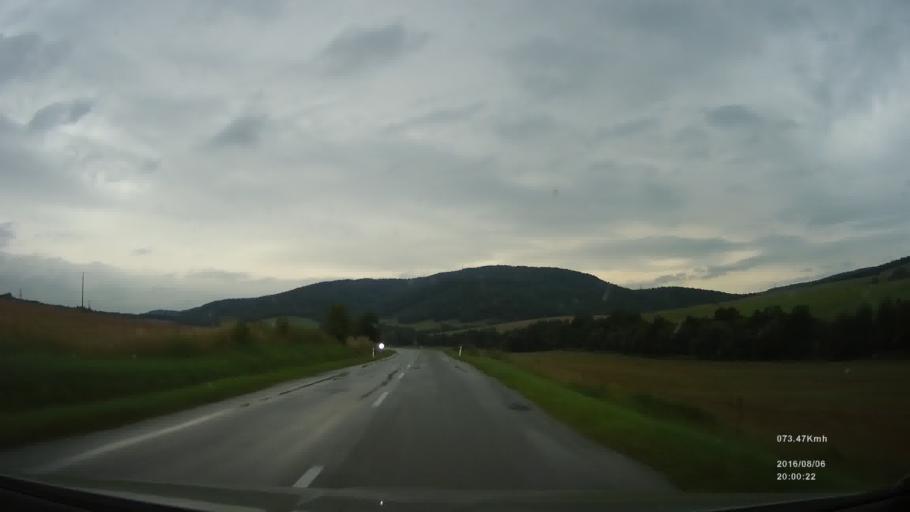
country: SK
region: Presovsky
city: Svidnik
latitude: 49.2532
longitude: 21.5814
